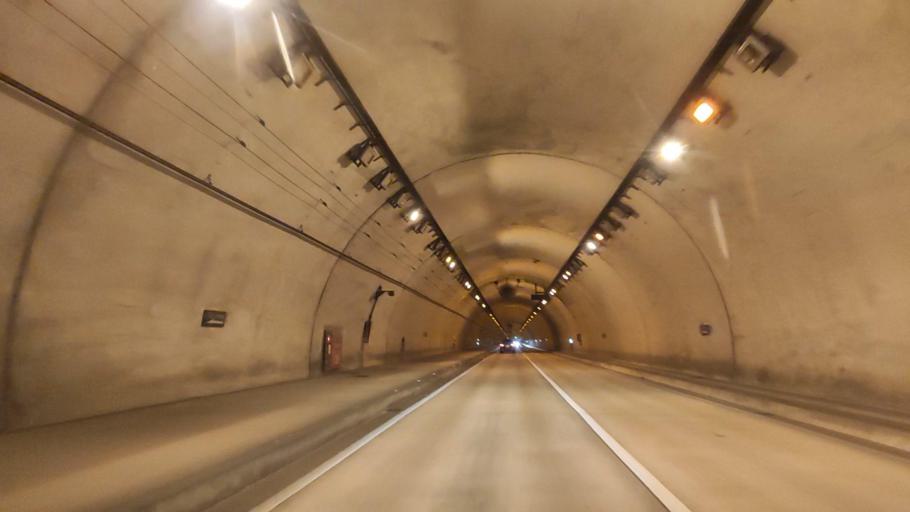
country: JP
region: Ehime
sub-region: Shikoku-chuo Shi
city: Matsuyama
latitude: 33.8766
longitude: 132.7140
